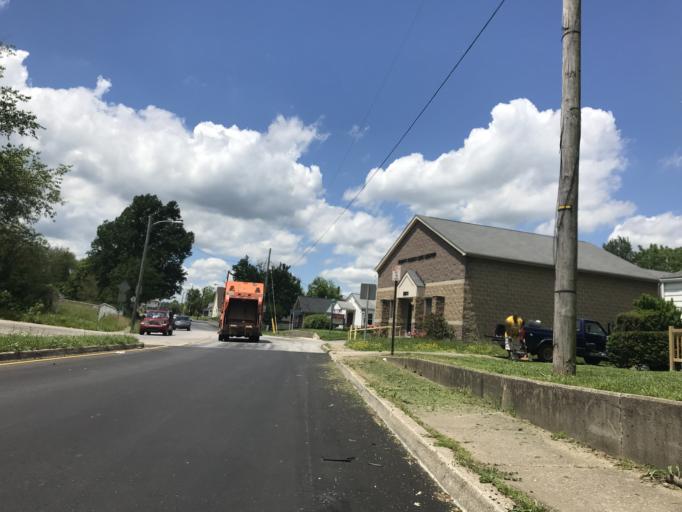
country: US
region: Kentucky
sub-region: Jefferson County
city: Shively
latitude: 38.2410
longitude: -85.8171
